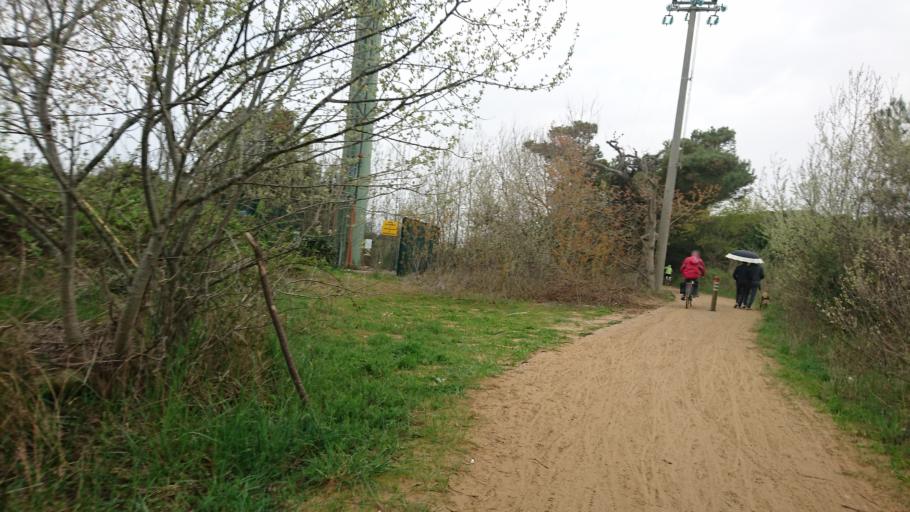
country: IT
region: Friuli Venezia Giulia
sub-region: Provincia di Udine
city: Lignano Sabbiadoro
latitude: 45.6363
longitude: 13.0966
